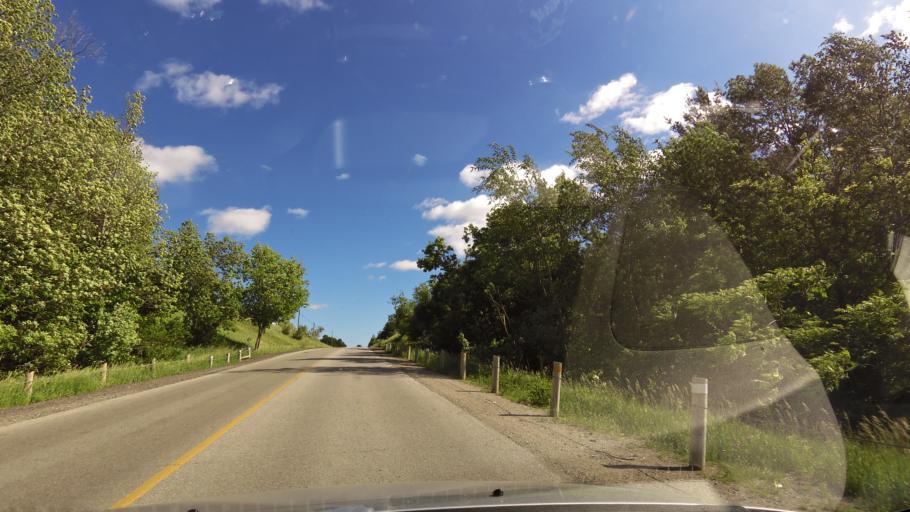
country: CA
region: Ontario
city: Bradford West Gwillimbury
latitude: 44.1667
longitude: -79.6168
